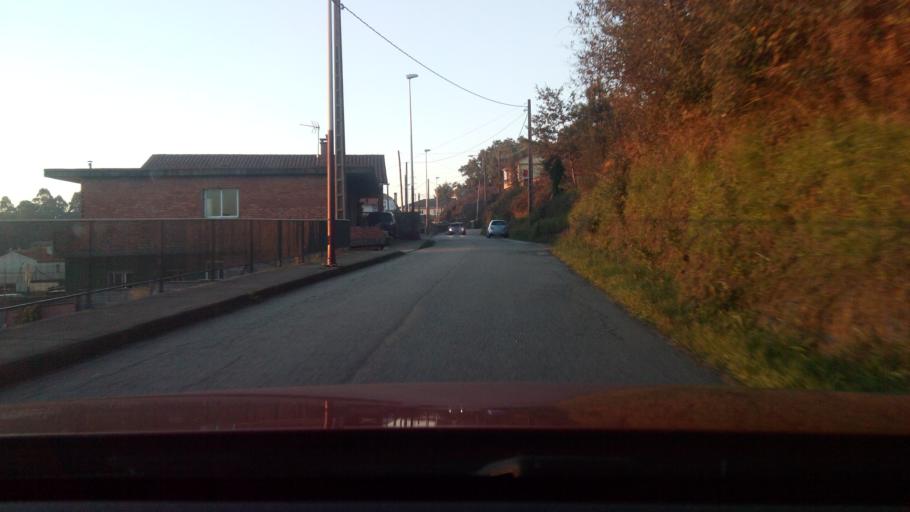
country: ES
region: Galicia
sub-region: Provincia de Pontevedra
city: Porrino
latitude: 42.1634
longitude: -8.6879
